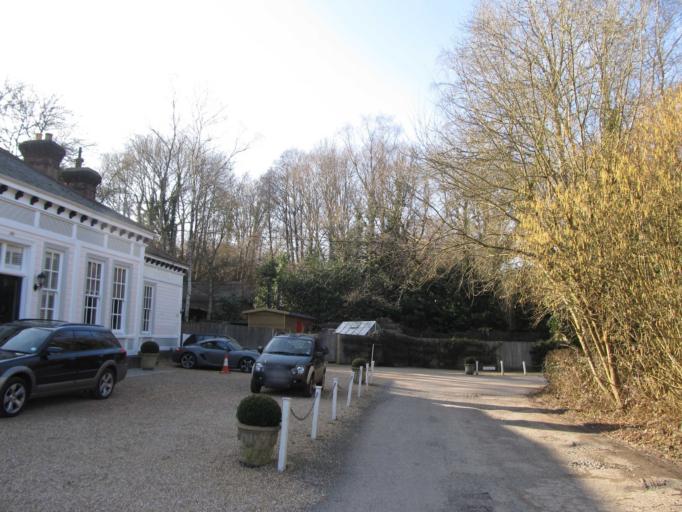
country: GB
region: England
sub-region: West Sussex
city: Petworth
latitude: 50.9638
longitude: -0.6200
